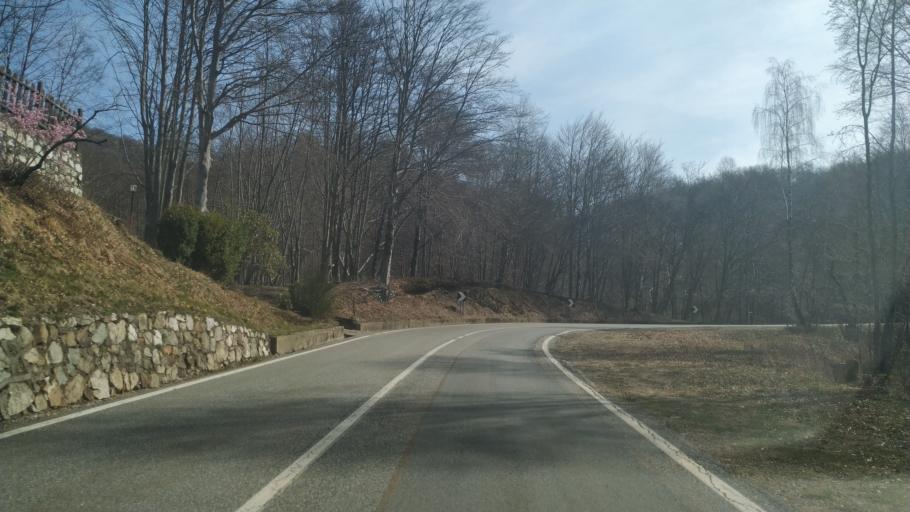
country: IT
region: Piedmont
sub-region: Provincia di Vercelli
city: Civiasco
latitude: 45.8089
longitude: 8.3172
